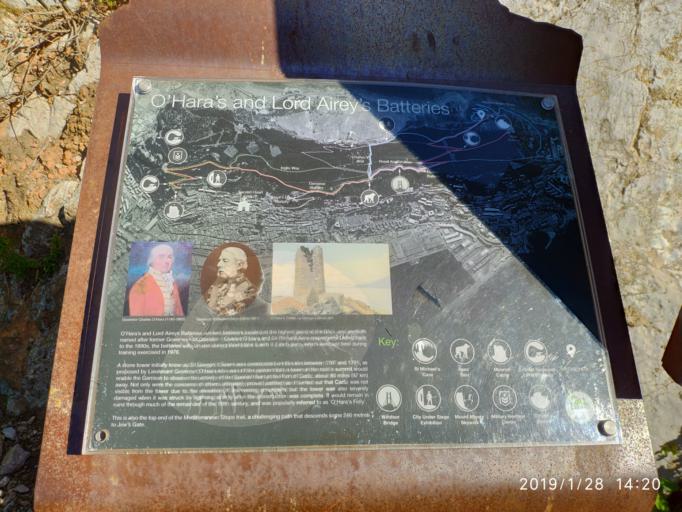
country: GI
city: Gibraltar
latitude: 36.1246
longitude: -5.3434
